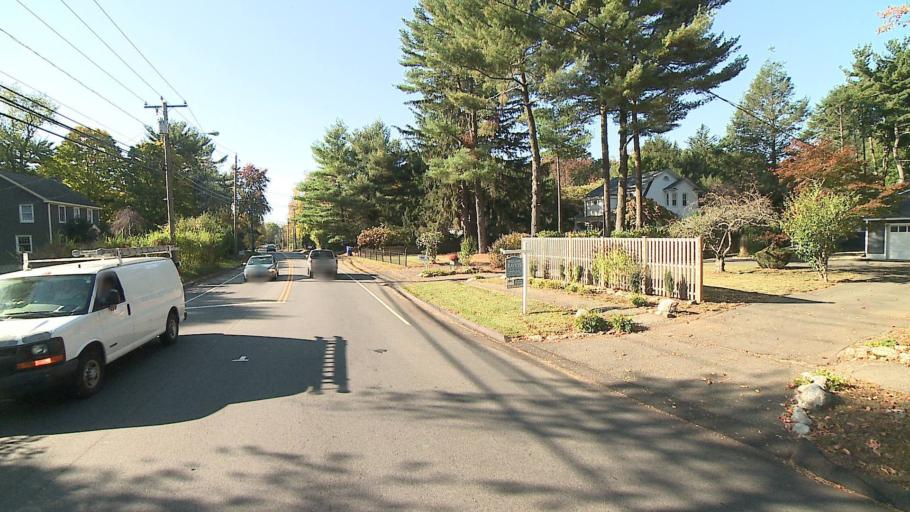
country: US
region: Connecticut
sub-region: Fairfield County
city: Norwalk
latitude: 41.1343
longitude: -73.4011
